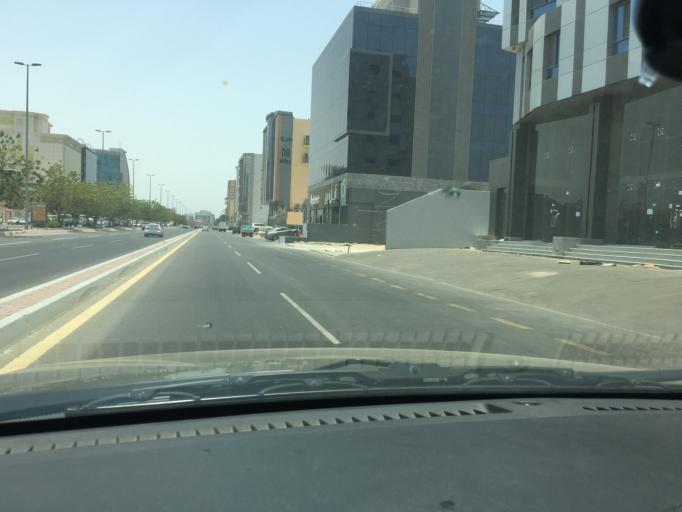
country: SA
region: Makkah
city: Jeddah
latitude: 21.6292
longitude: 39.1345
